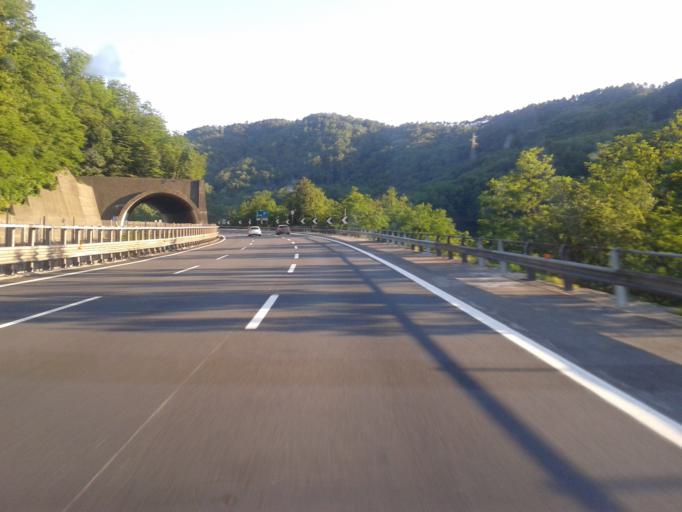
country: IT
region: Piedmont
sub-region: Provincia di Alessandria
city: Belforte Monferrato
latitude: 44.6194
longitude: 8.6560
